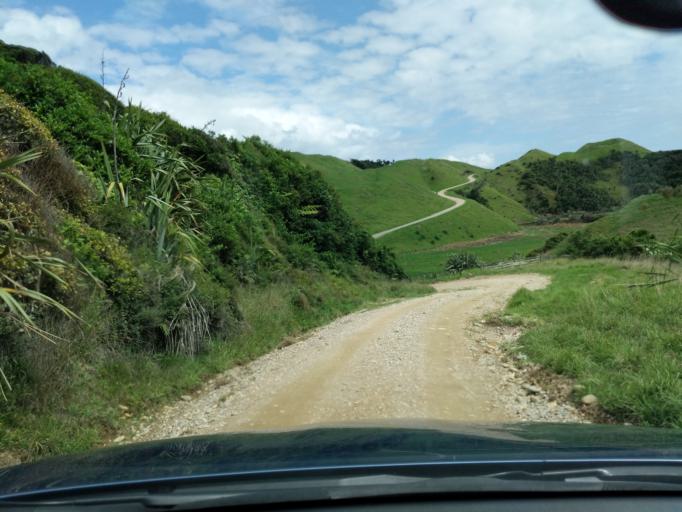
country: NZ
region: Tasman
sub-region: Tasman District
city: Takaka
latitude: -40.6704
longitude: 172.3995
